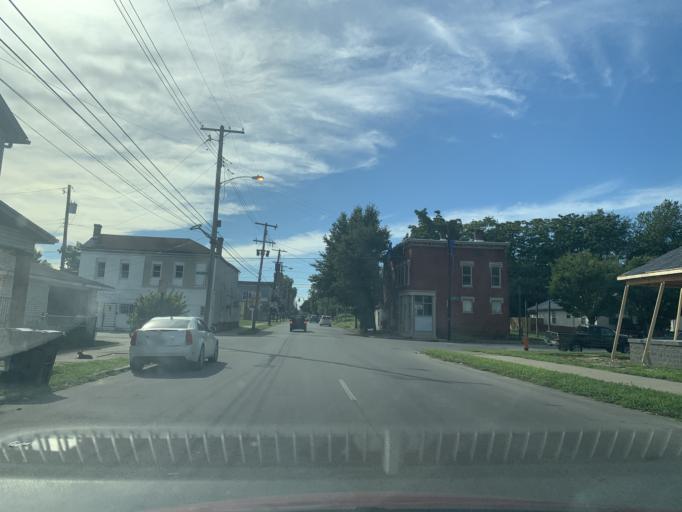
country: US
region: Kentucky
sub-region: Jefferson County
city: Louisville
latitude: 38.2541
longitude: -85.7842
